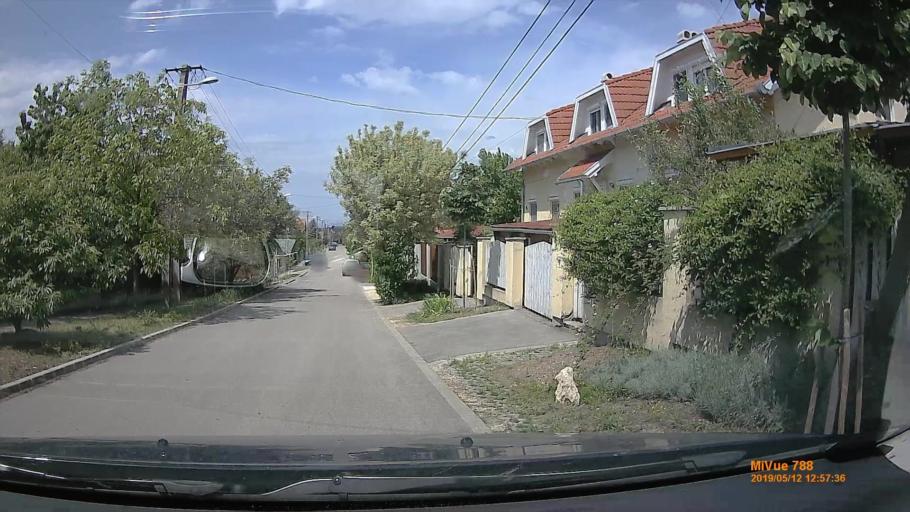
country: HU
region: Pest
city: Ecser
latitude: 47.4737
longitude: 19.2986
